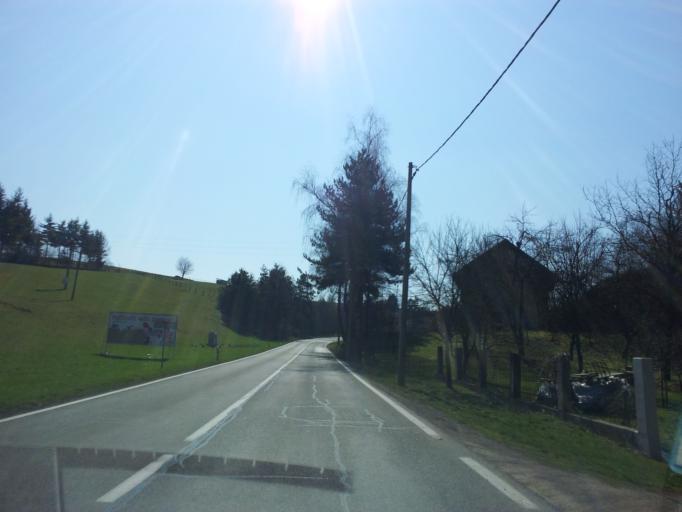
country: HR
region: Licko-Senjska
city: Jezerce
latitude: 44.9910
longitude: 15.6480
